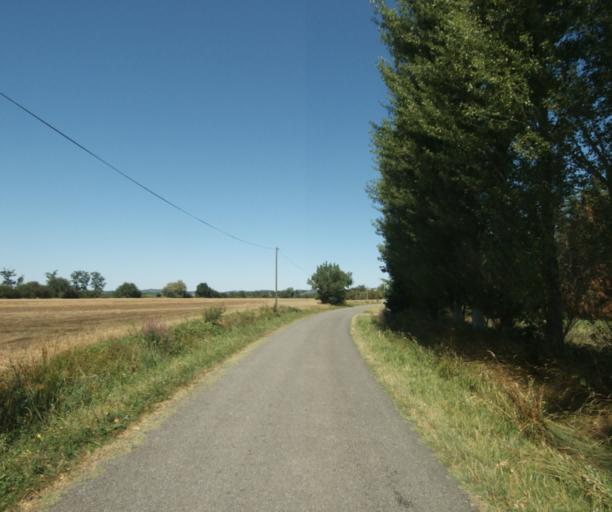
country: FR
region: Midi-Pyrenees
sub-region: Departement de la Haute-Garonne
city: Revel
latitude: 43.4754
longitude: 1.9798
